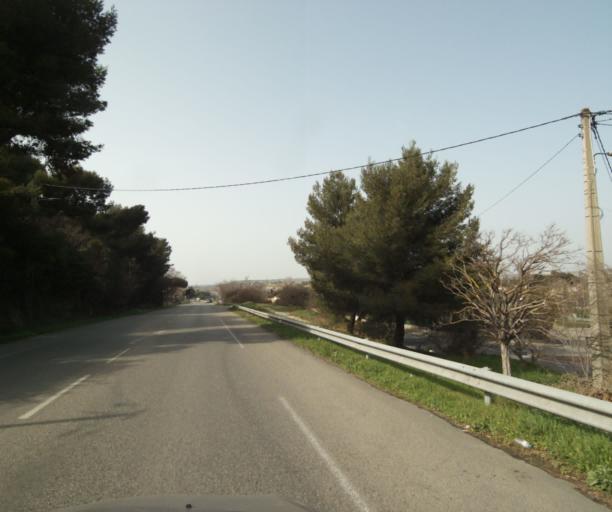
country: FR
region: Provence-Alpes-Cote d'Azur
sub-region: Departement des Bouches-du-Rhone
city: Les Pennes-Mirabeau
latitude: 43.4135
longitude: 5.3006
